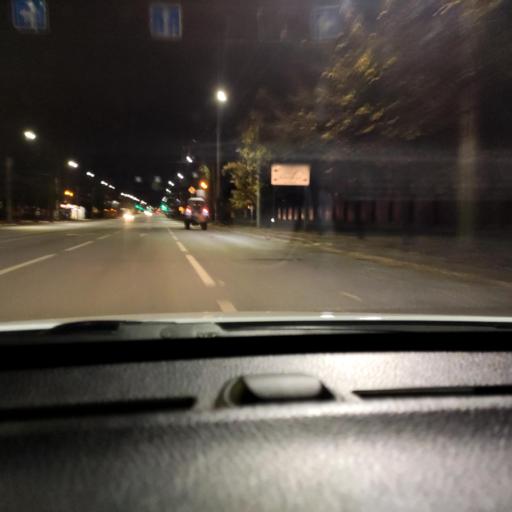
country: RU
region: Voronezj
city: Voronezh
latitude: 51.6785
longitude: 39.2594
